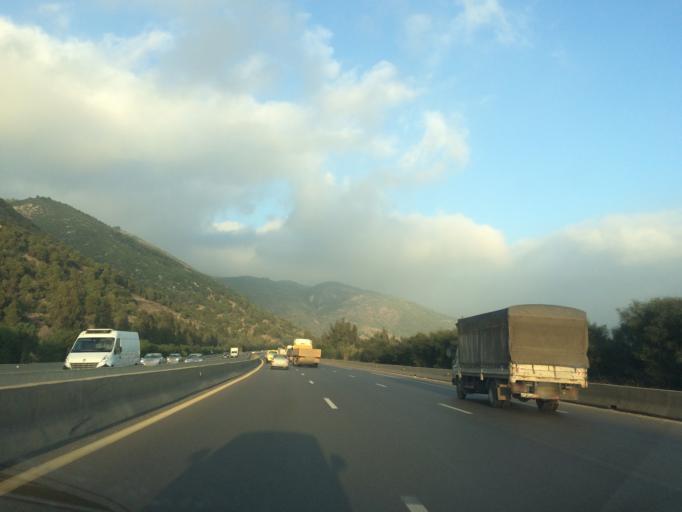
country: DZ
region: Tipaza
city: Hadjout
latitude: 36.3855
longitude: 2.4910
